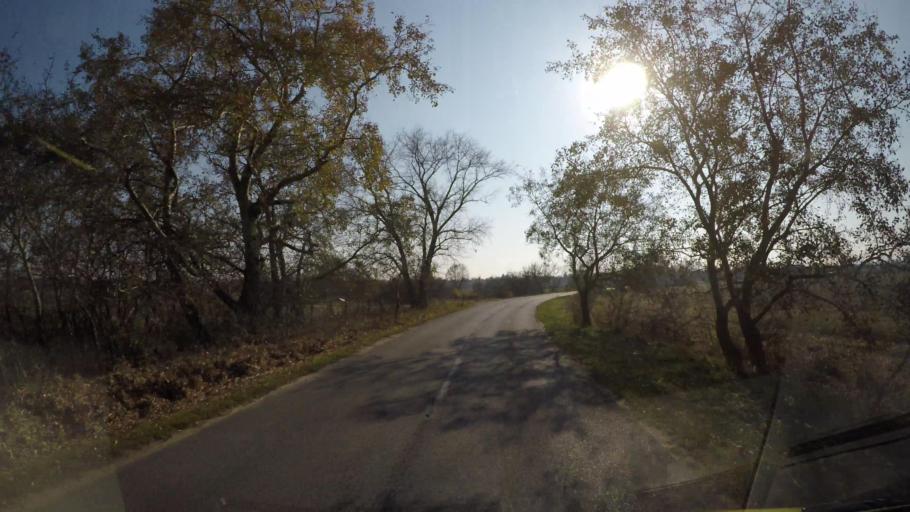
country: HU
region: Pest
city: Leanyfalu
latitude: 47.6956
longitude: 19.1041
